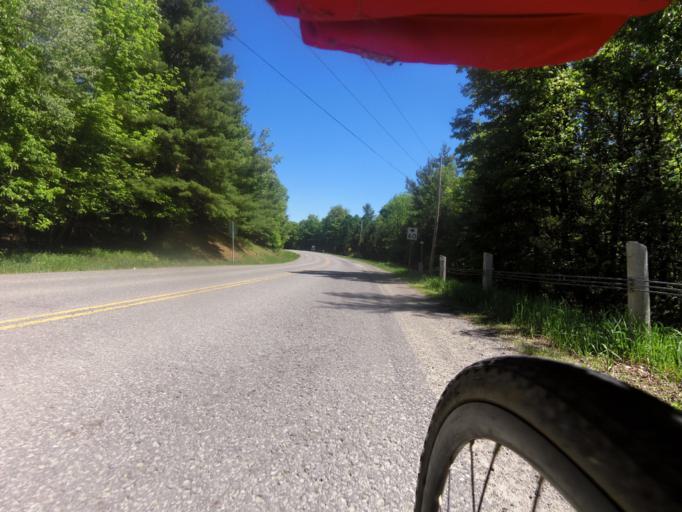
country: CA
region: Ontario
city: Carleton Place
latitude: 45.1859
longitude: -76.3445
